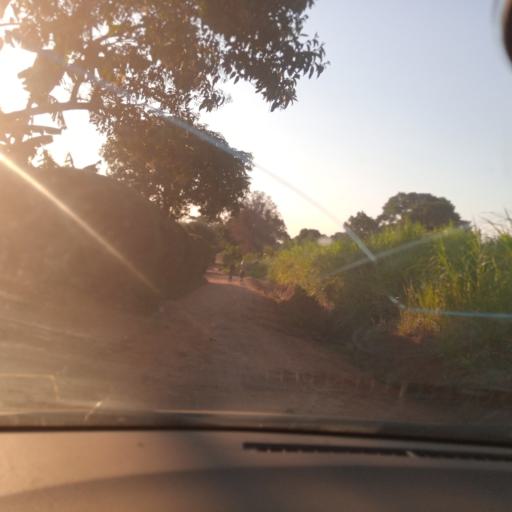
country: UG
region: Central Region
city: Masaka
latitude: -0.3339
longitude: 31.7563
